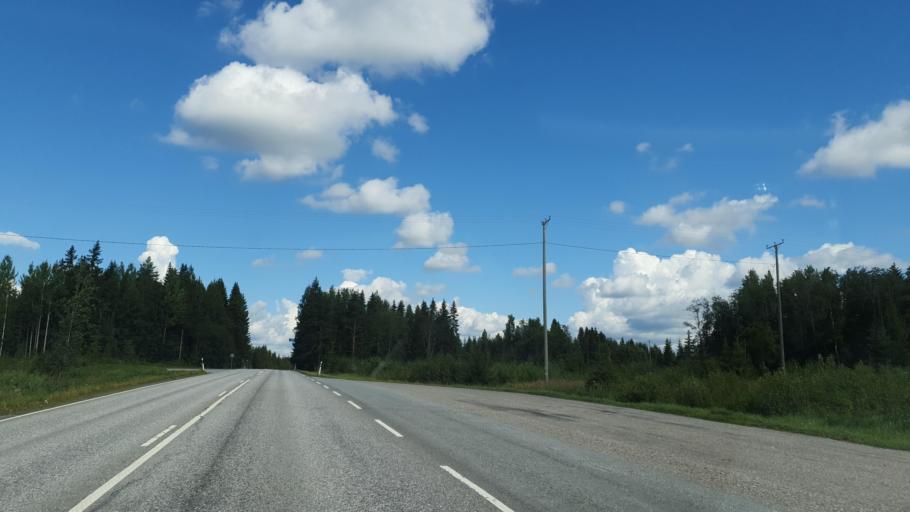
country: FI
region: Northern Savo
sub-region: Ylae-Savo
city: Sonkajaervi
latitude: 63.7439
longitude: 27.3827
